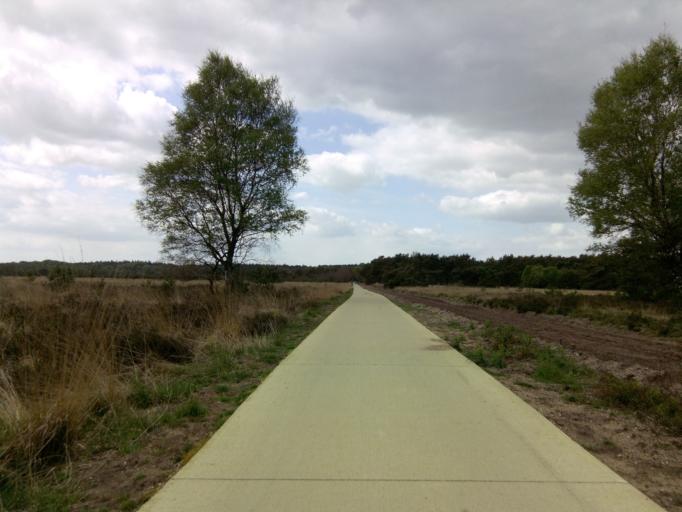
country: NL
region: Gelderland
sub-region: Gemeente Ede
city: Wekerom
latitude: 52.0632
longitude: 5.7052
